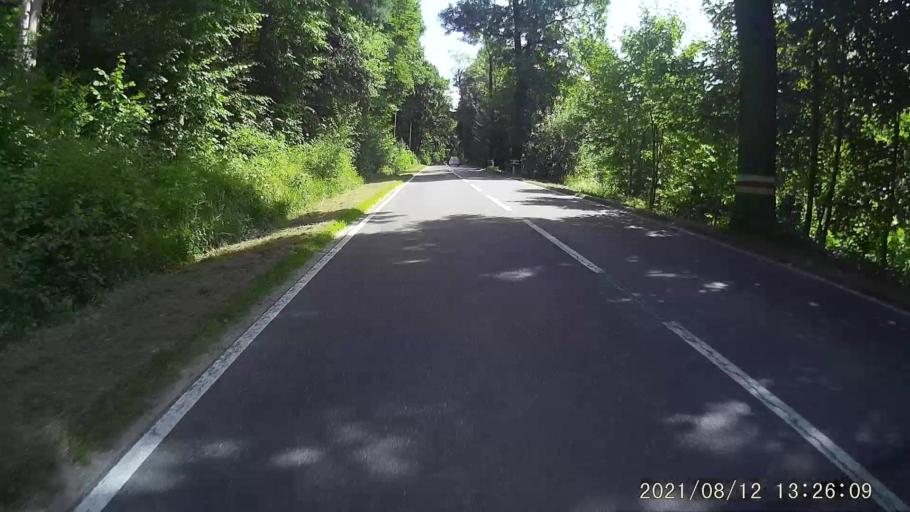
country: PL
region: Lower Silesian Voivodeship
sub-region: Powiat klodzki
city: Ladek-Zdroj
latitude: 50.3263
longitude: 16.8821
